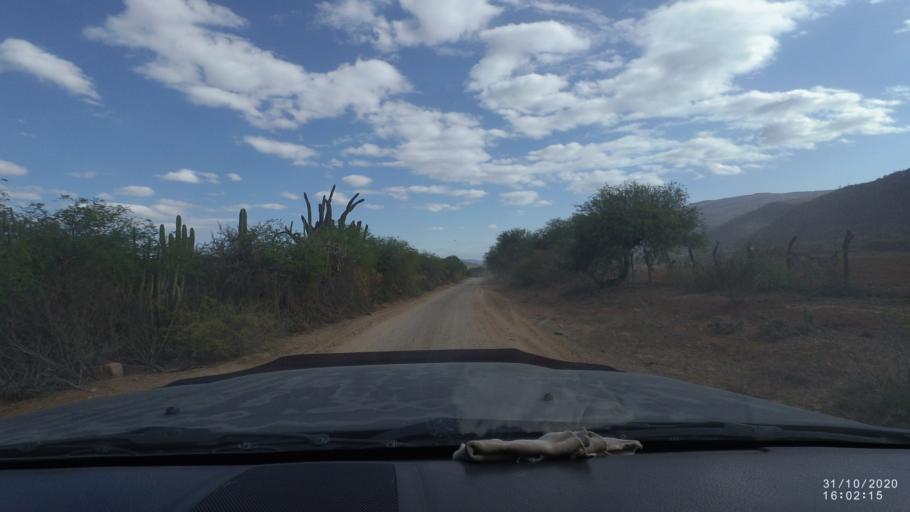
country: BO
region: Chuquisaca
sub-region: Provincia Zudanez
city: Mojocoya
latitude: -18.3456
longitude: -64.6573
